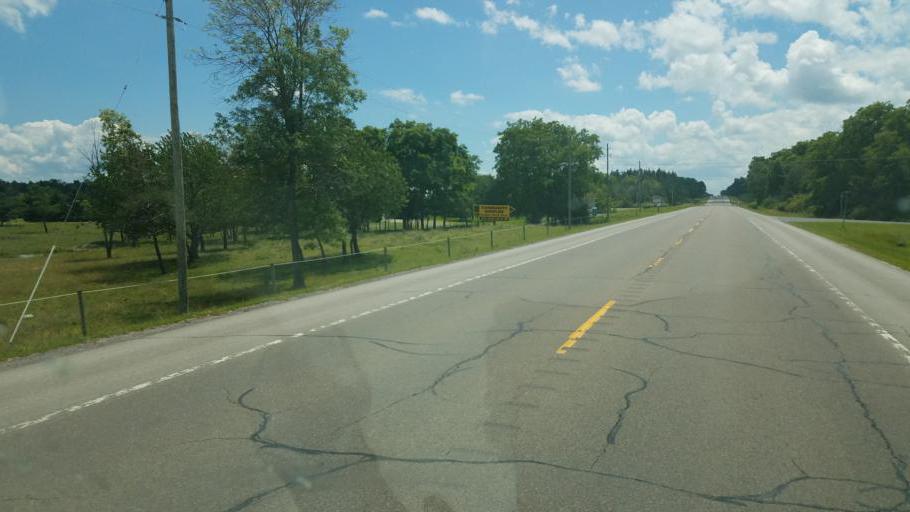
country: US
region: New York
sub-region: Yates County
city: Keuka Park
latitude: 42.5874
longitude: -77.0368
